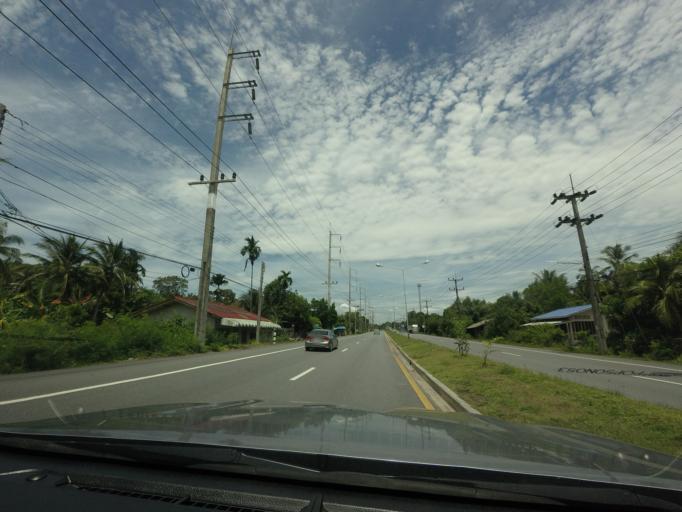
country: TH
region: Songkhla
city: Krasae Sin
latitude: 7.5747
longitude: 100.4093
